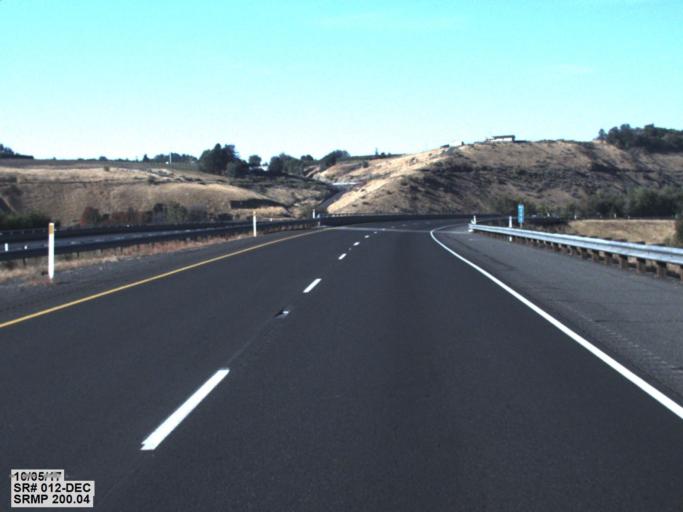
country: US
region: Washington
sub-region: Yakima County
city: Selah
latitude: 46.6228
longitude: -120.5623
